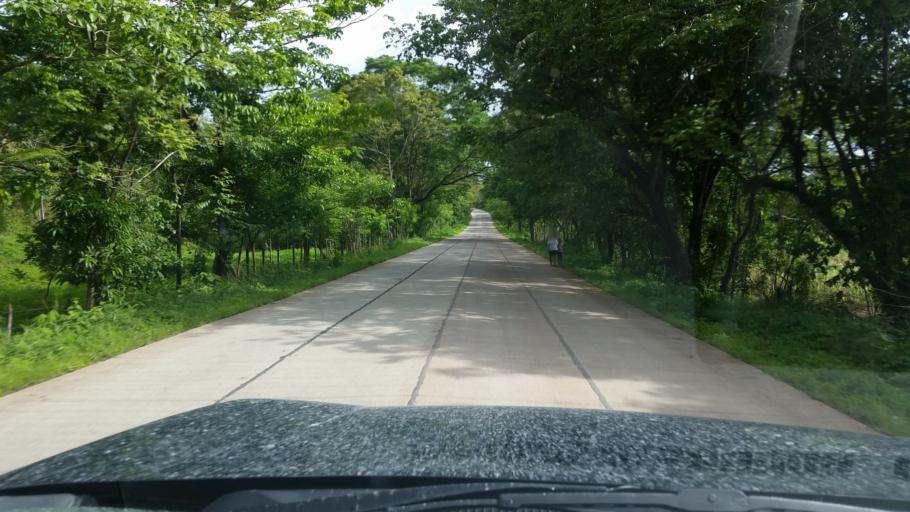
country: NI
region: Atlantico Norte (RAAN)
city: Siuna
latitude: 13.5814
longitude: -84.8145
